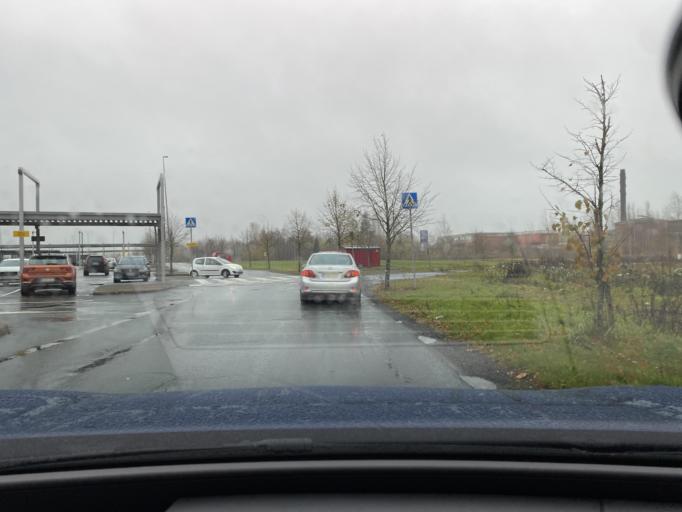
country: FI
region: Haeme
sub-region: Forssa
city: Forssa
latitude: 60.8112
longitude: 23.6341
